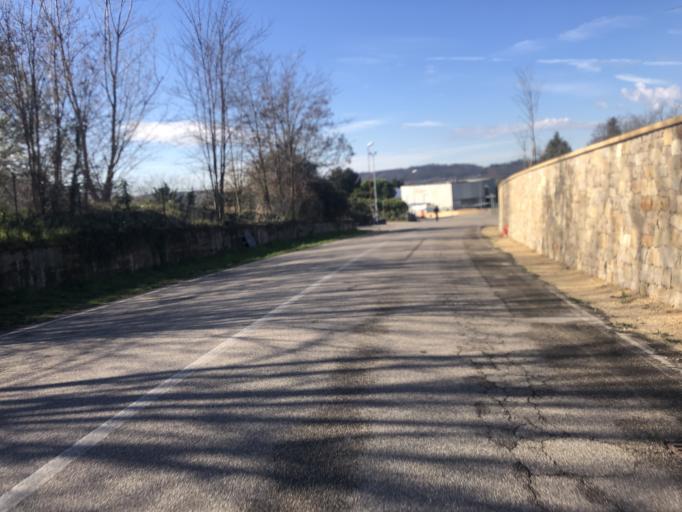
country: IT
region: Veneto
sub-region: Provincia di Verona
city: Sant'Ambrogio di Valpollicella
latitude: 45.5165
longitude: 10.8367
